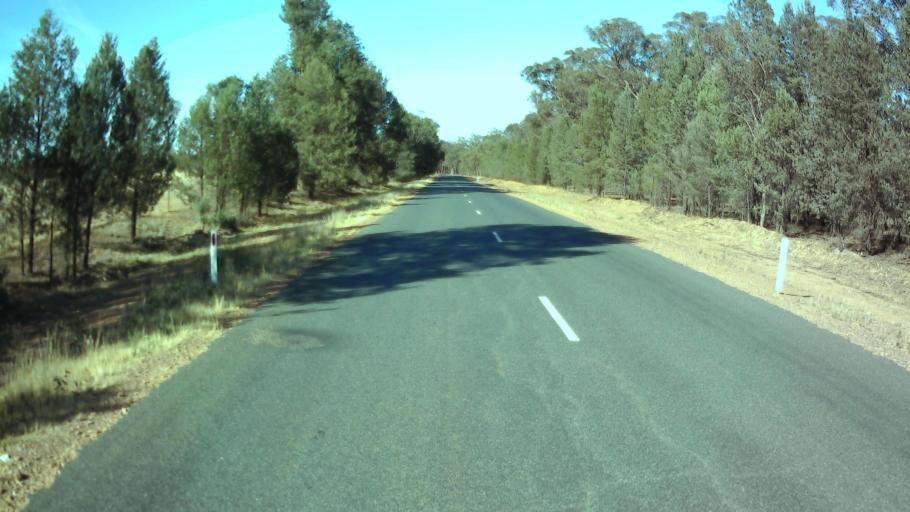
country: AU
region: New South Wales
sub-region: Weddin
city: Grenfell
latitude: -34.0199
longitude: 148.1037
